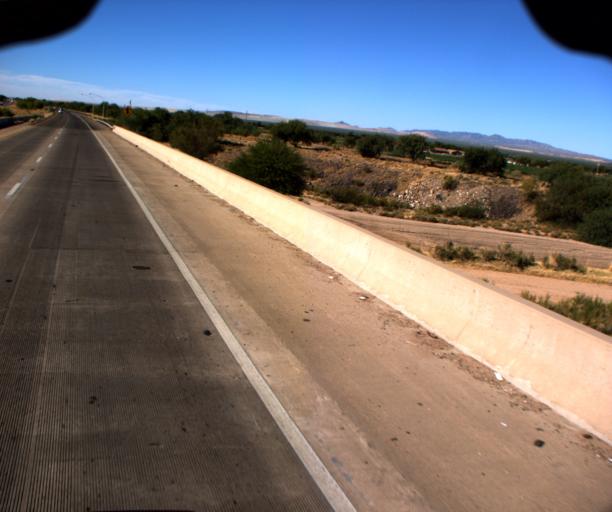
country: US
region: Arizona
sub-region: Pima County
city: Drexel Heights
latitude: 32.1046
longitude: -110.9933
